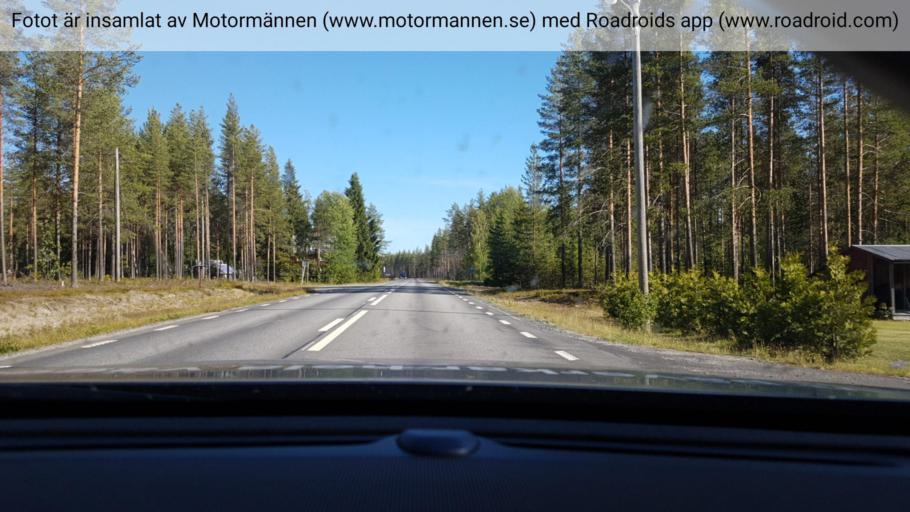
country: SE
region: Vaesterbotten
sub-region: Lycksele Kommun
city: Lycksele
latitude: 64.5312
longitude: 18.7678
